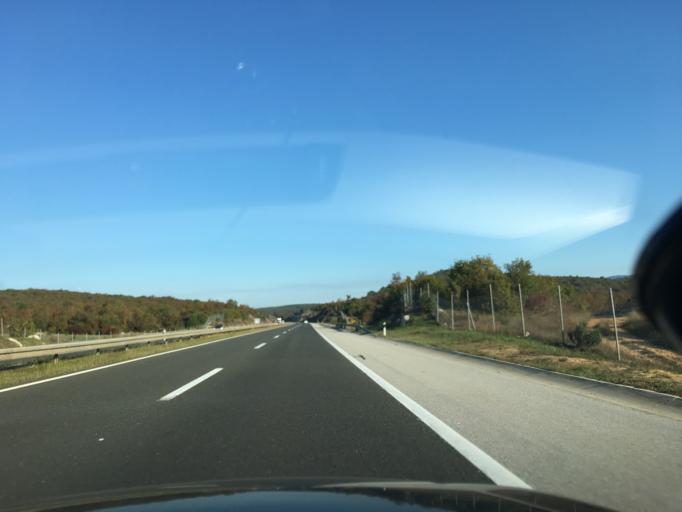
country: HR
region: Licko-Senjska
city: Gospic
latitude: 44.6837
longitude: 15.4076
